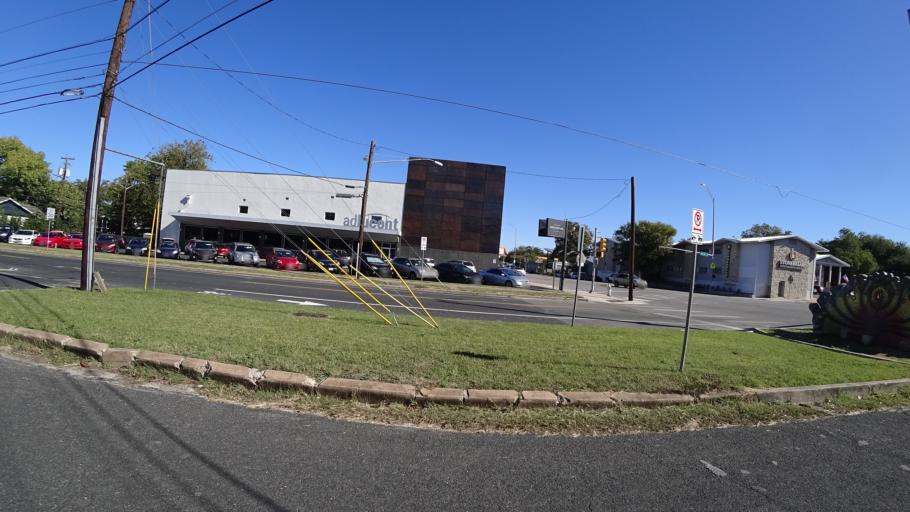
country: US
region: Texas
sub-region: Travis County
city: Austin
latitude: 30.2419
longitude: -97.7529
